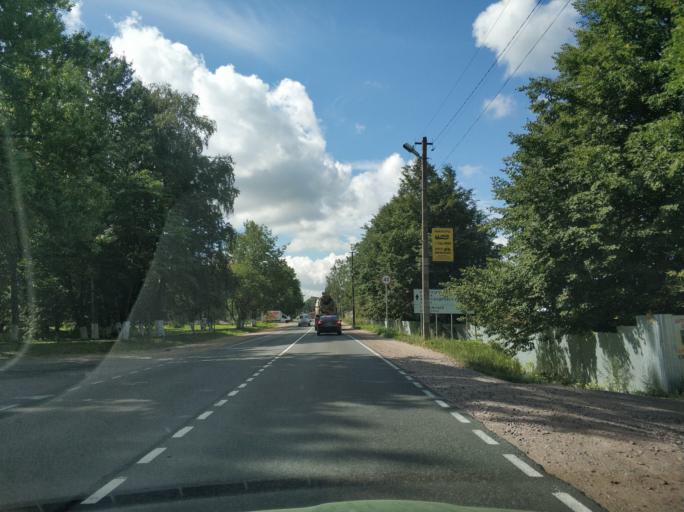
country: RU
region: Leningrad
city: Romanovka
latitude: 60.0478
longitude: 30.7035
